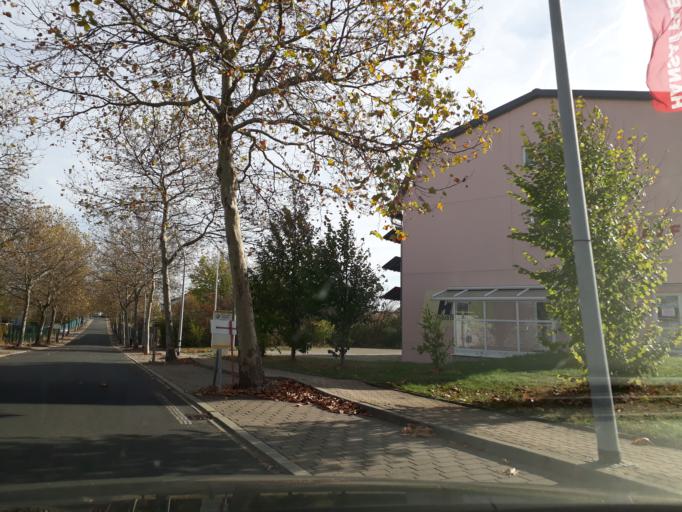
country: DE
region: Saxony
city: Niederstriegis
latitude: 51.1173
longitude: 13.1501
